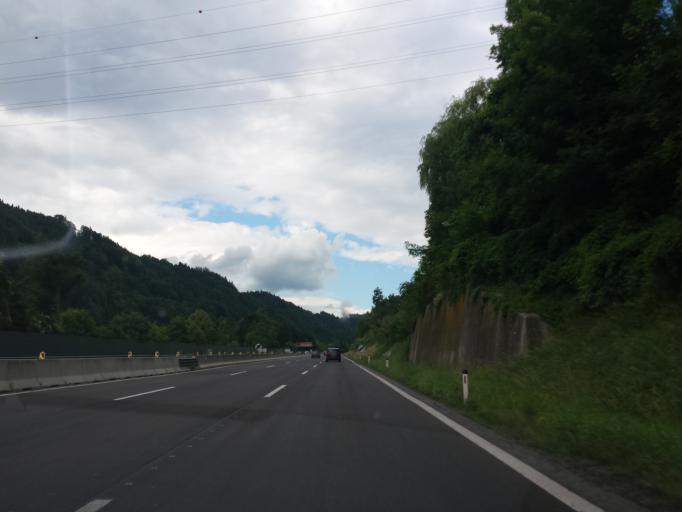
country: AT
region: Styria
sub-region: Politischer Bezirk Bruck-Muerzzuschlag
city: Bruck an der Mur
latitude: 47.4140
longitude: 15.2878
